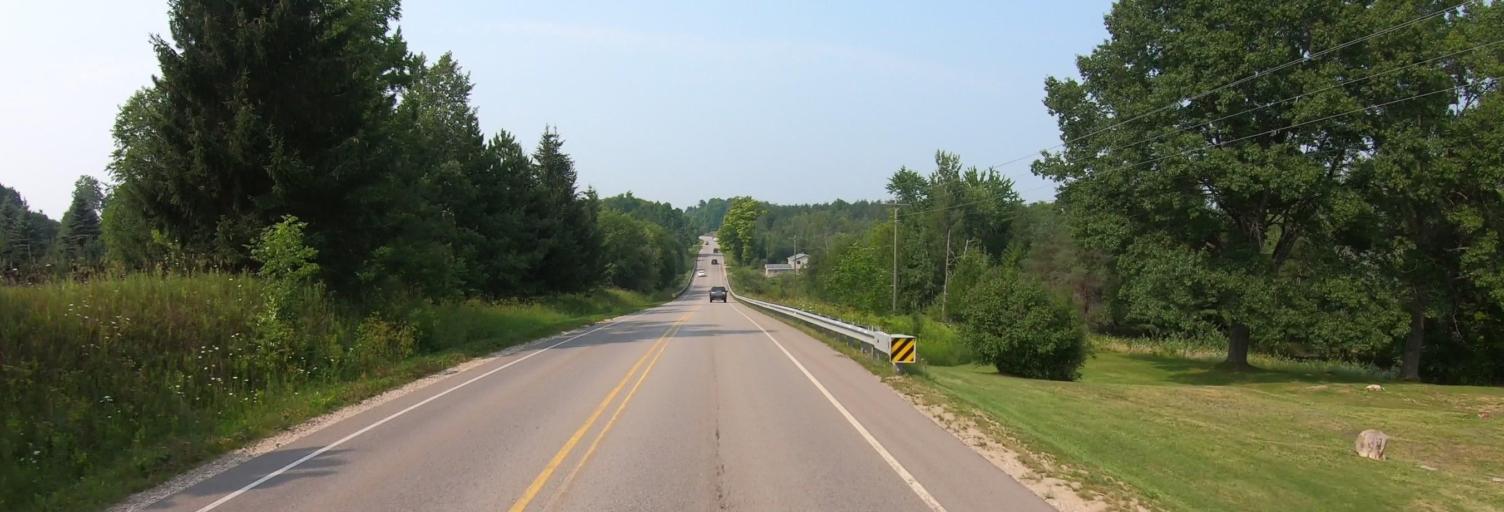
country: US
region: Michigan
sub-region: Charlevoix County
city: Charlevoix
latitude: 45.1880
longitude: -85.2635
